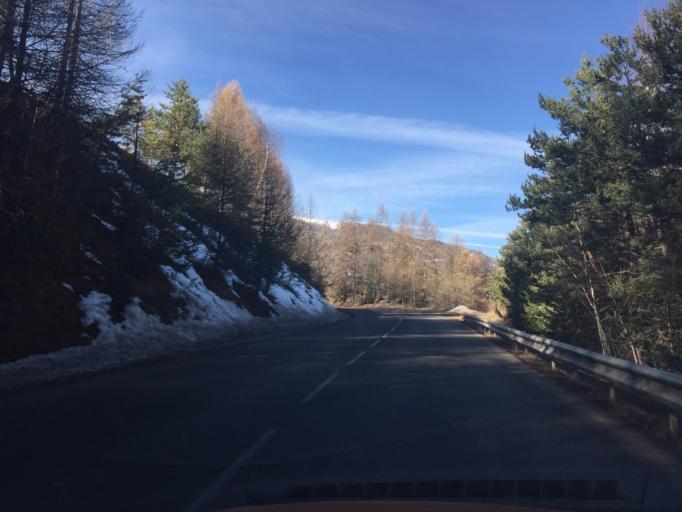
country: FR
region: Provence-Alpes-Cote d'Azur
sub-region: Departement des Hautes-Alpes
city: Embrun
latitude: 44.5097
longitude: 6.5625
